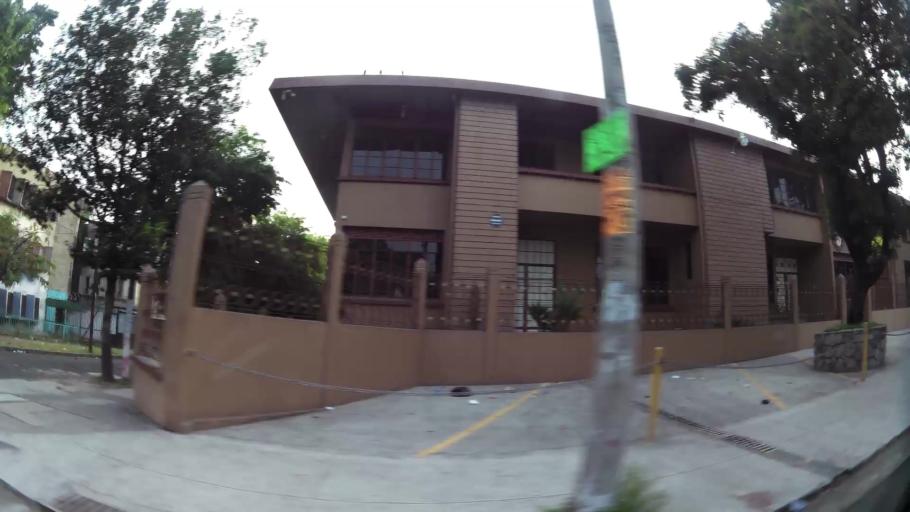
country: SV
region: San Salvador
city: San Salvador
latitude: 13.7050
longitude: -89.1908
